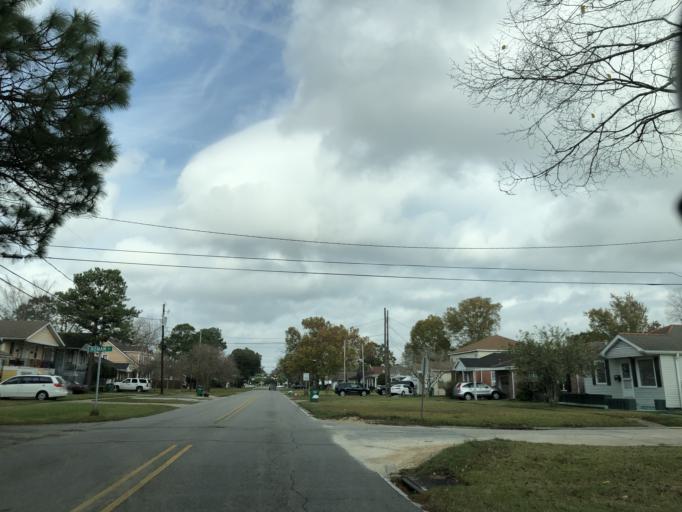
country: US
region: Louisiana
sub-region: Jefferson Parish
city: Metairie Terrace
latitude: 29.9788
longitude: -90.1604
